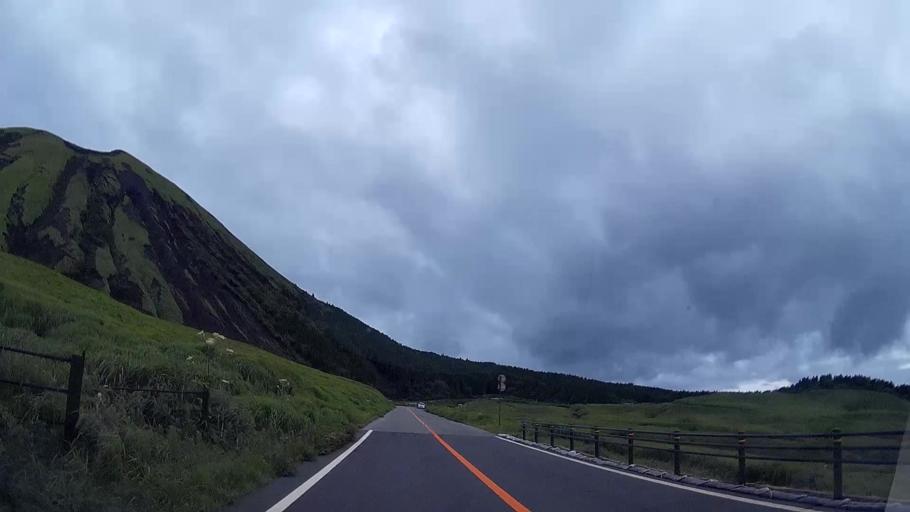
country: JP
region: Kumamoto
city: Aso
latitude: 32.9010
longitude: 131.0518
